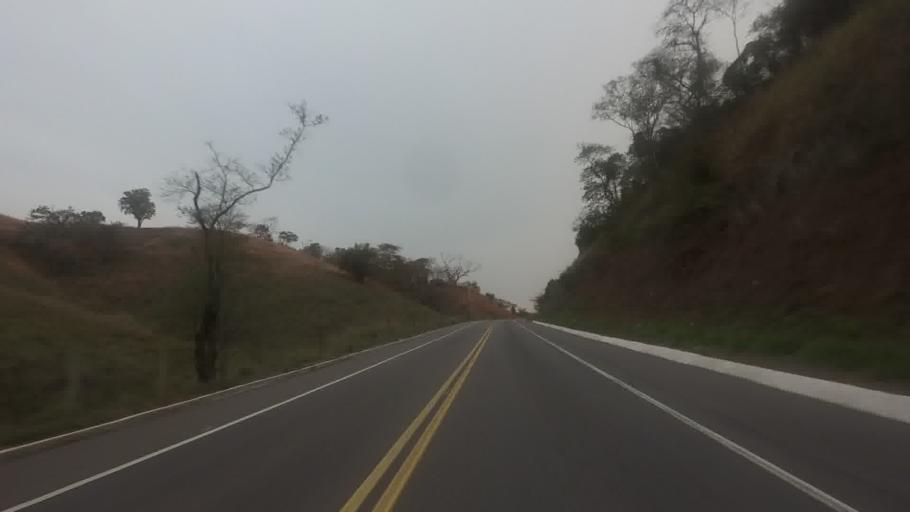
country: BR
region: Minas Gerais
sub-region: Recreio
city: Recreio
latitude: -21.7113
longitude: -42.4260
